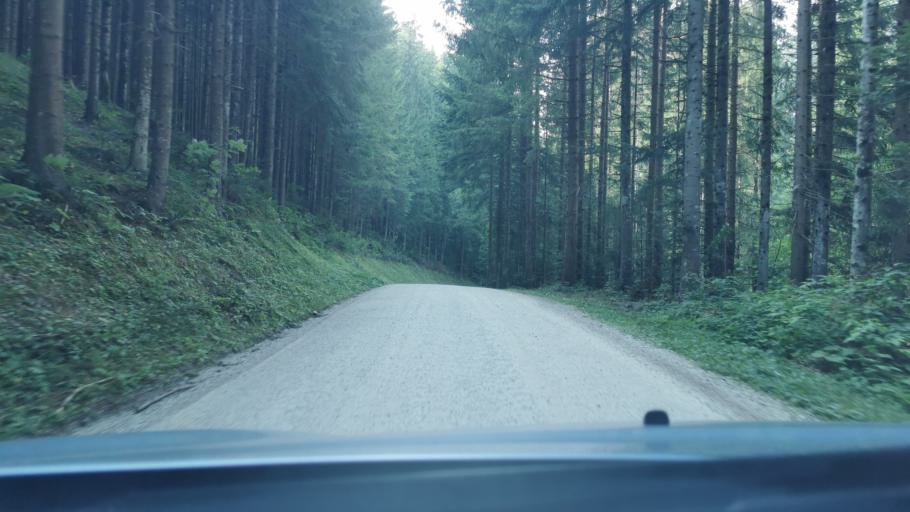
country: AT
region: Styria
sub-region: Politischer Bezirk Weiz
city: Fischbach
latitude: 47.3970
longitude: 15.6532
